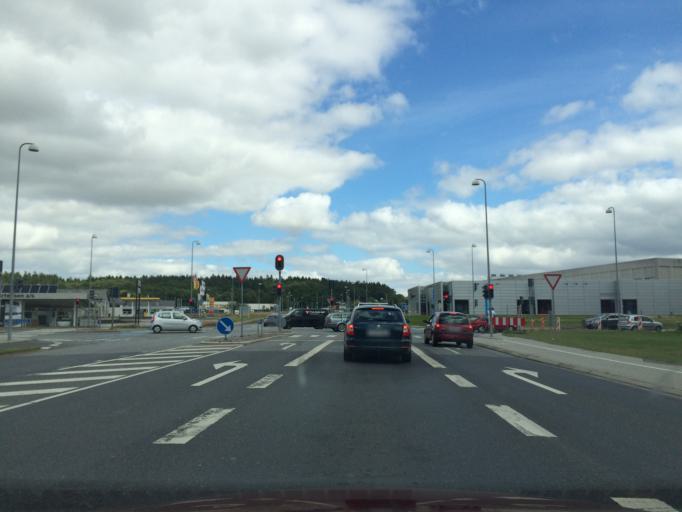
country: DK
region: Central Jutland
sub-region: Silkeborg Kommune
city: Silkeborg
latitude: 56.1851
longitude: 9.5725
